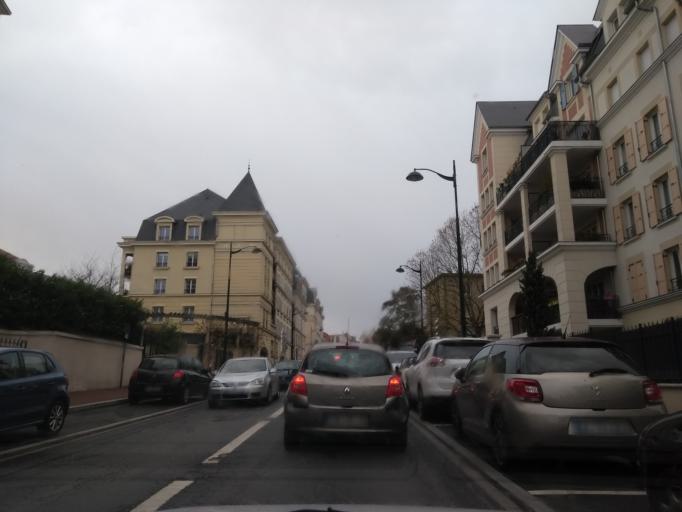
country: FR
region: Ile-de-France
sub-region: Departement des Hauts-de-Seine
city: Le Plessis-Robinson
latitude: 48.7800
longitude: 2.2593
